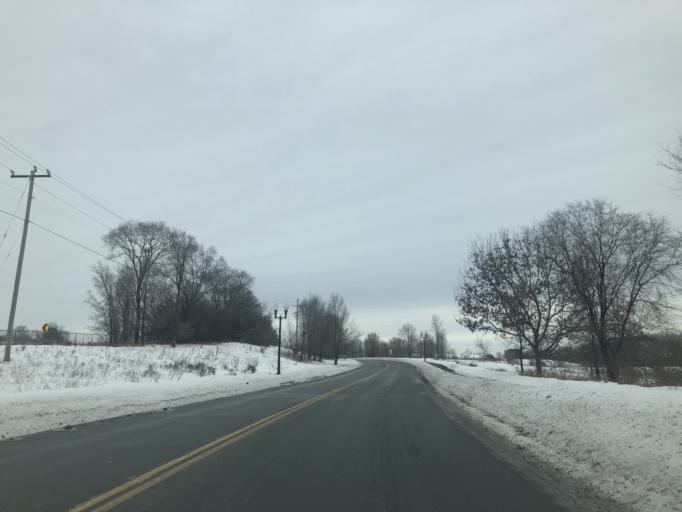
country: US
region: Minnesota
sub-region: Ramsey County
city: Mounds View
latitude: 45.1118
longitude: -93.1873
